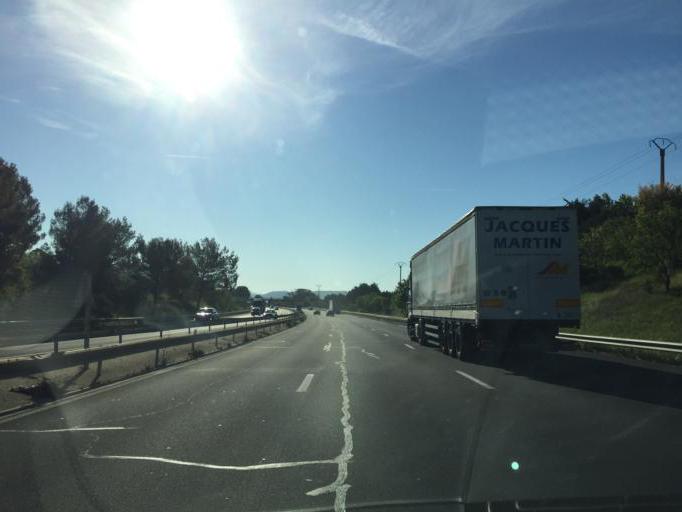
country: FR
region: Provence-Alpes-Cote d'Azur
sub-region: Departement des Bouches-du-Rhone
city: Aix-en-Provence
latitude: 43.5216
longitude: 5.4129
